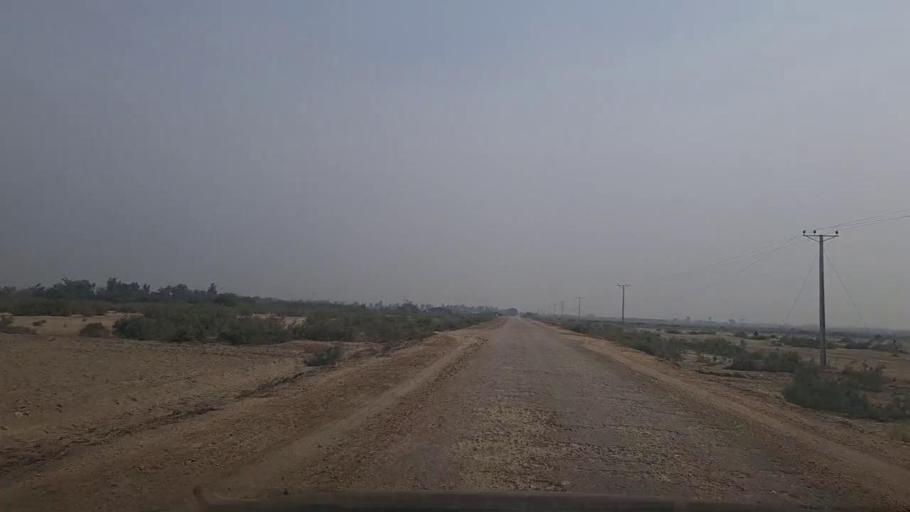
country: PK
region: Sindh
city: Mirpur Sakro
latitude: 24.4587
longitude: 67.6983
